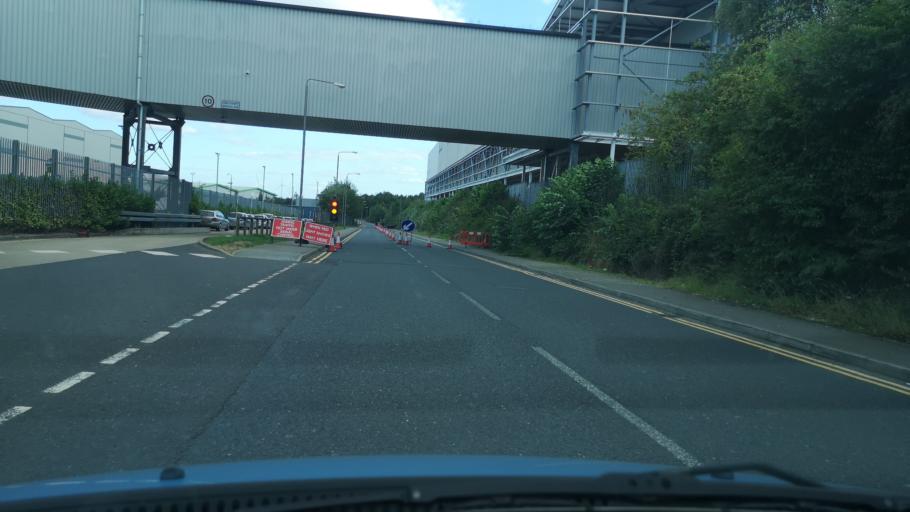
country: GB
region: England
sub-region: City and Borough of Wakefield
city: South Elmsall
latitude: 53.6033
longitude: -1.2711
